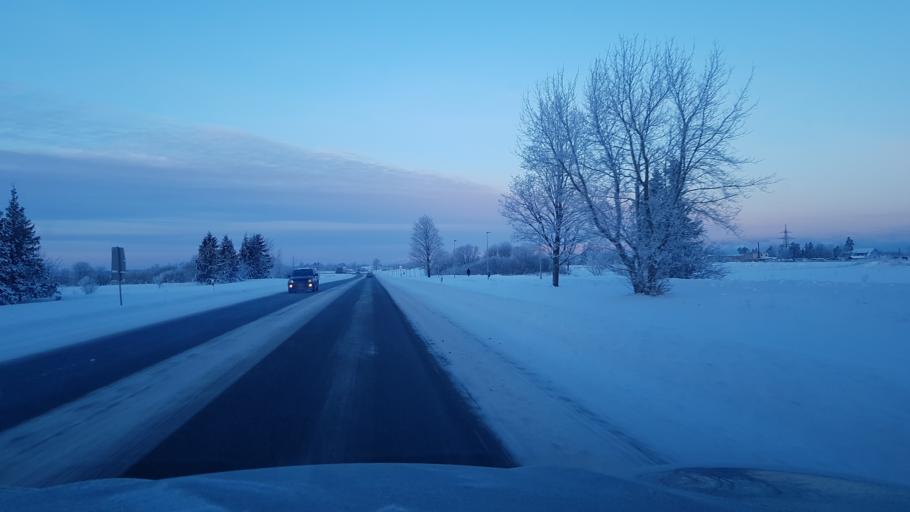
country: EE
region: Ida-Virumaa
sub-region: Narva linn
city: Narva
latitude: 59.3879
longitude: 28.1435
